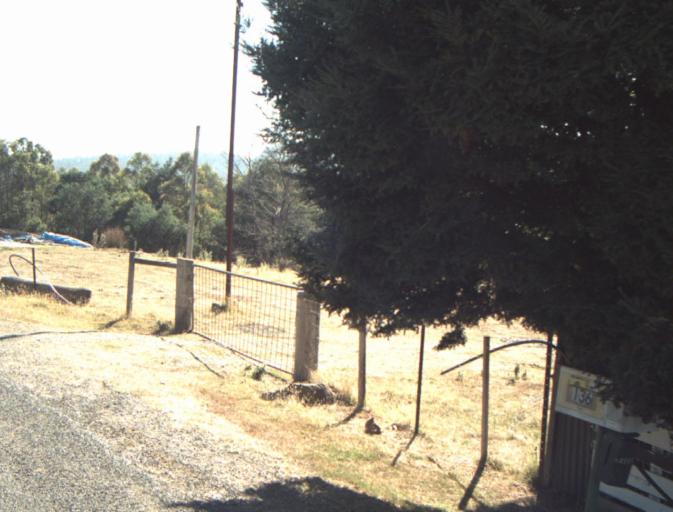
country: AU
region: Tasmania
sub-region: Dorset
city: Scottsdale
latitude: -41.2890
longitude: 147.3602
